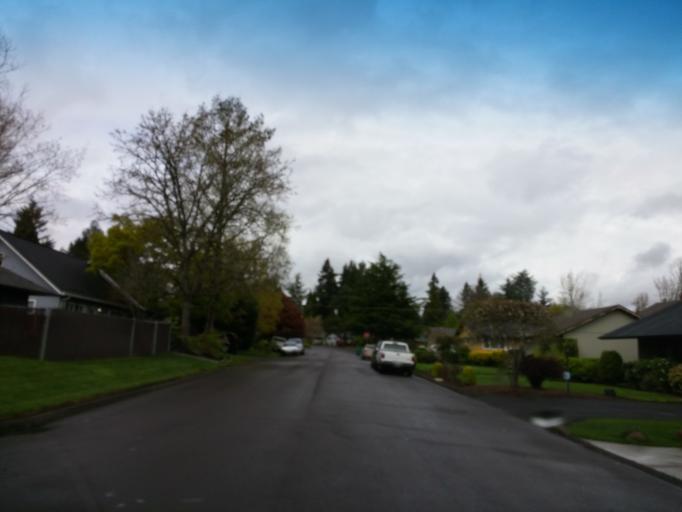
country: US
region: Oregon
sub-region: Washington County
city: Cedar Mill
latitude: 45.5161
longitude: -122.8257
